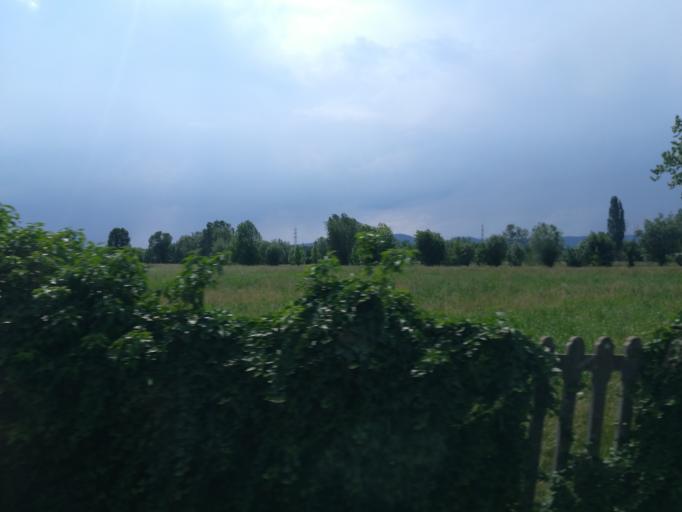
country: IT
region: Veneto
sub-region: Provincia di Vicenza
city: Dueville
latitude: 45.6398
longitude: 11.5415
